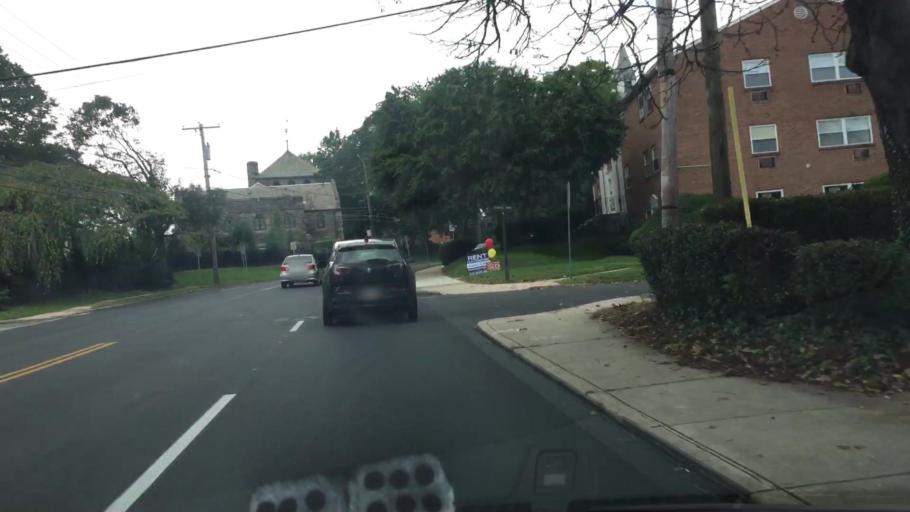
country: US
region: Pennsylvania
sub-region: Montgomery County
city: Bala-Cynwyd
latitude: 40.0058
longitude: -75.2340
